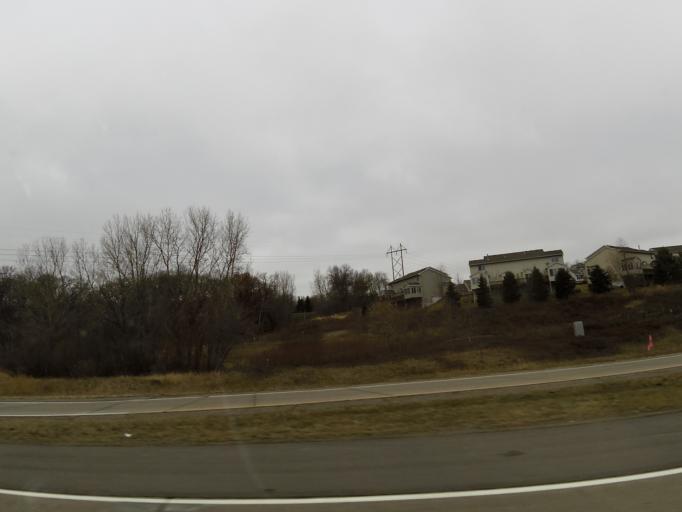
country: US
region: Minnesota
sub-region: Dakota County
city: Burnsville
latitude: 44.7577
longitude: -93.2518
